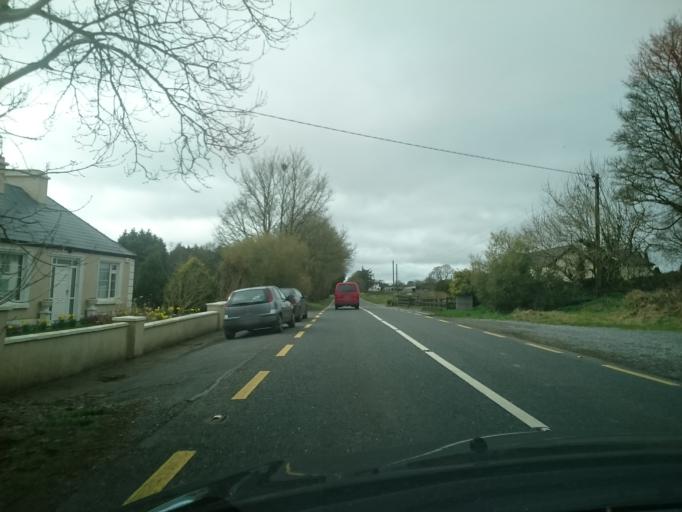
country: IE
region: Connaught
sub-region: Maigh Eo
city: Ballyhaunis
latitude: 53.7513
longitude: -8.7890
